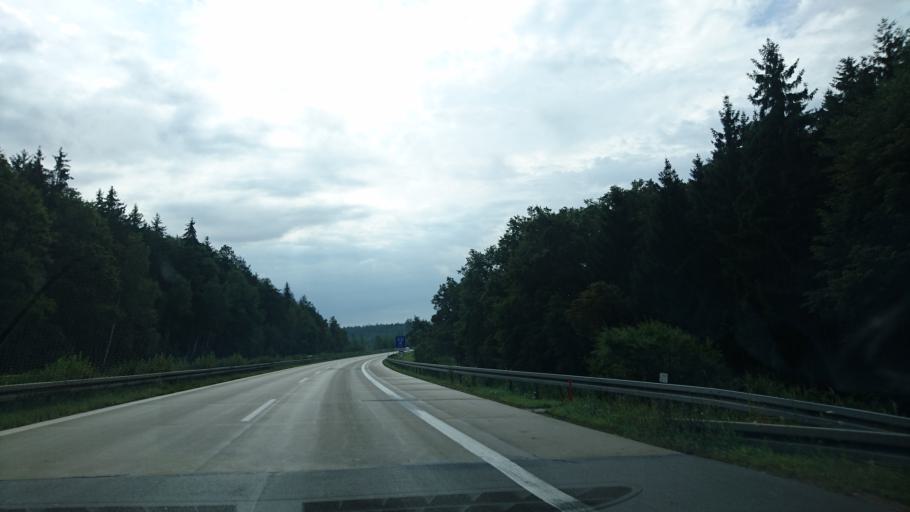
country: DE
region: Bavaria
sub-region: Upper Palatinate
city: Pentling
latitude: 48.9675
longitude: 12.0830
